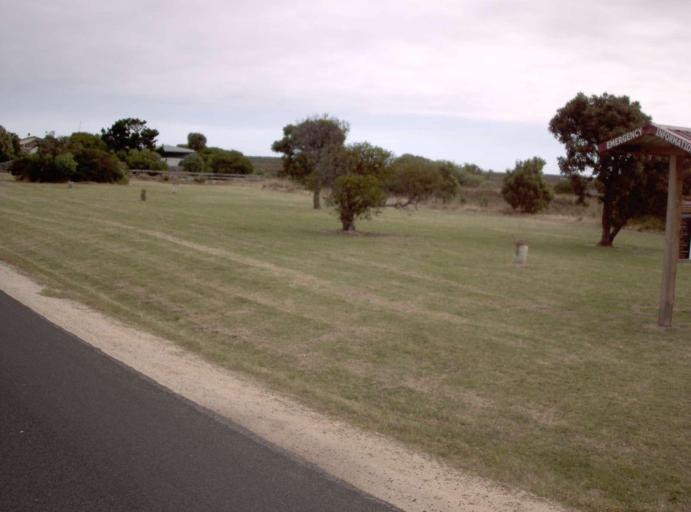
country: AU
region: Victoria
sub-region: Wellington
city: Sale
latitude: -38.6057
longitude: 146.8895
